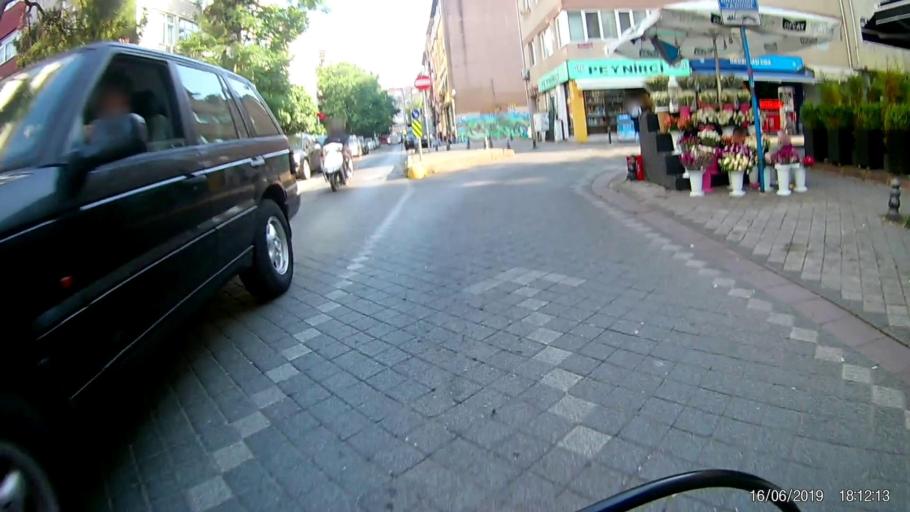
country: TR
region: Istanbul
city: UEskuedar
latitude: 40.9867
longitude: 29.0311
